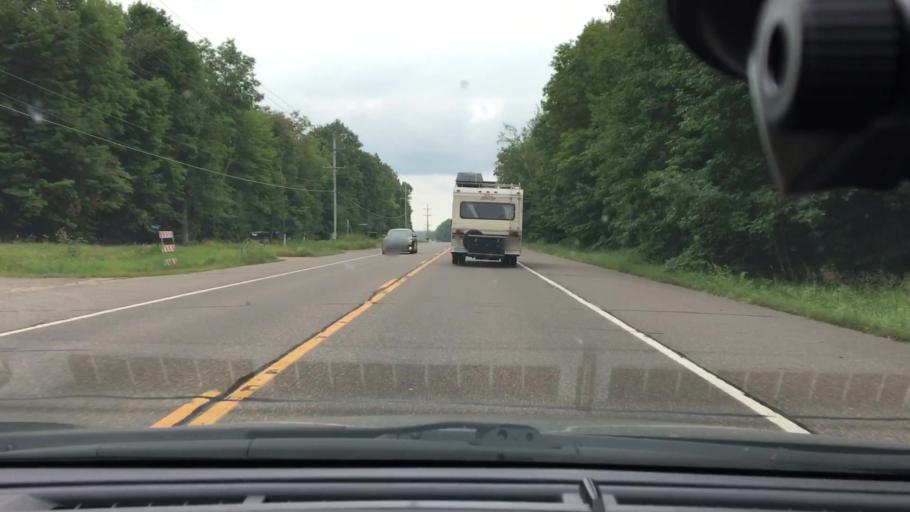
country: US
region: Minnesota
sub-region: Crow Wing County
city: Crosby
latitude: 46.4902
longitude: -93.9132
